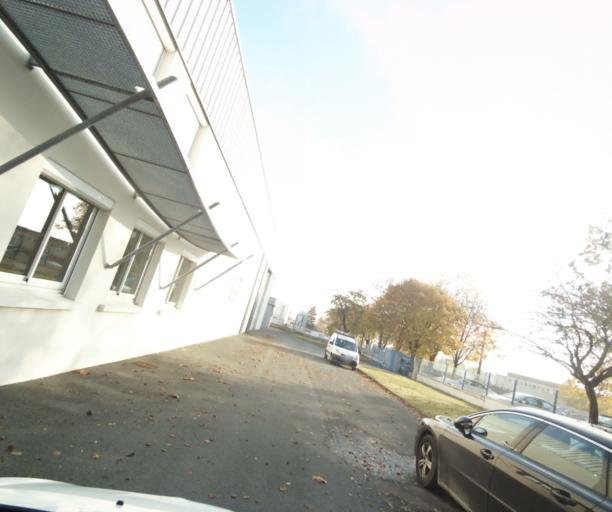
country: FR
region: Poitou-Charentes
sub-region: Departement de la Charente-Maritime
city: Saintes
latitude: 45.7464
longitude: -0.6672
